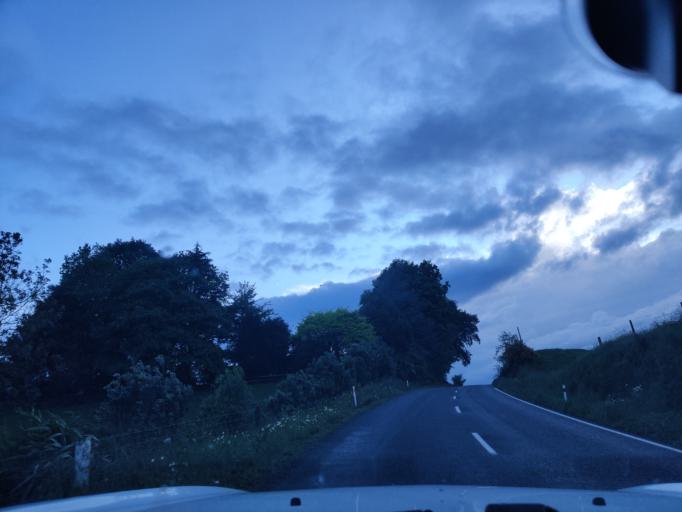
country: NZ
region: Waikato
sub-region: South Waikato District
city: Tokoroa
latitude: -38.2041
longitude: 175.8149
